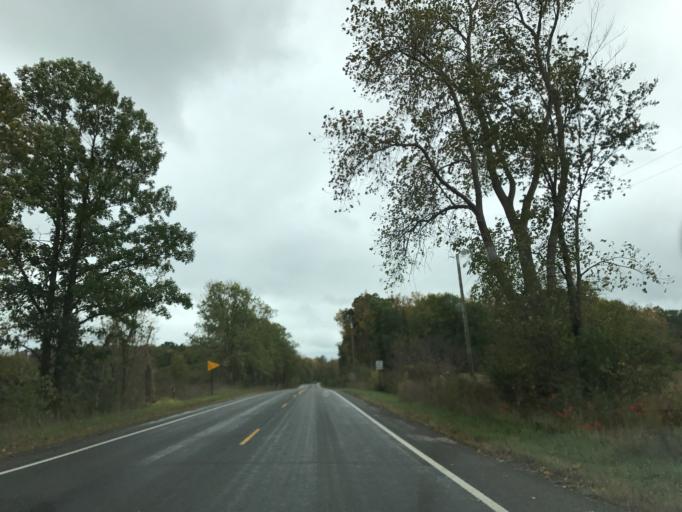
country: US
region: Michigan
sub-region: Washtenaw County
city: Ann Arbor
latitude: 42.3446
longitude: -83.6621
